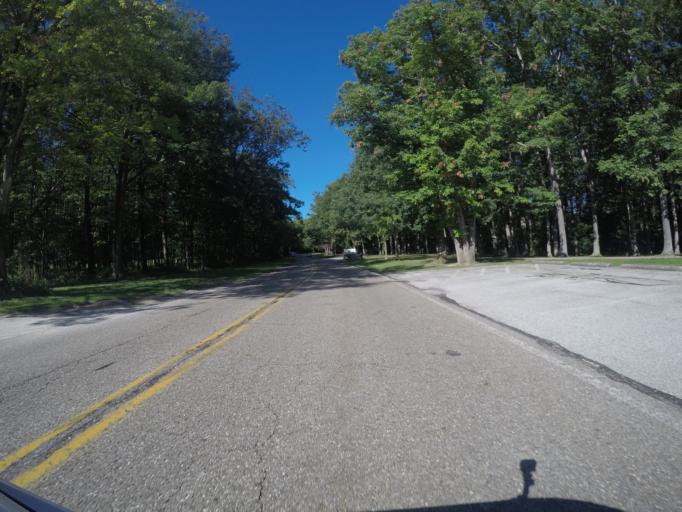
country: US
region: Ohio
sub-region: Cuyahoga County
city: Brecksville
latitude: 41.3191
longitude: -81.6171
